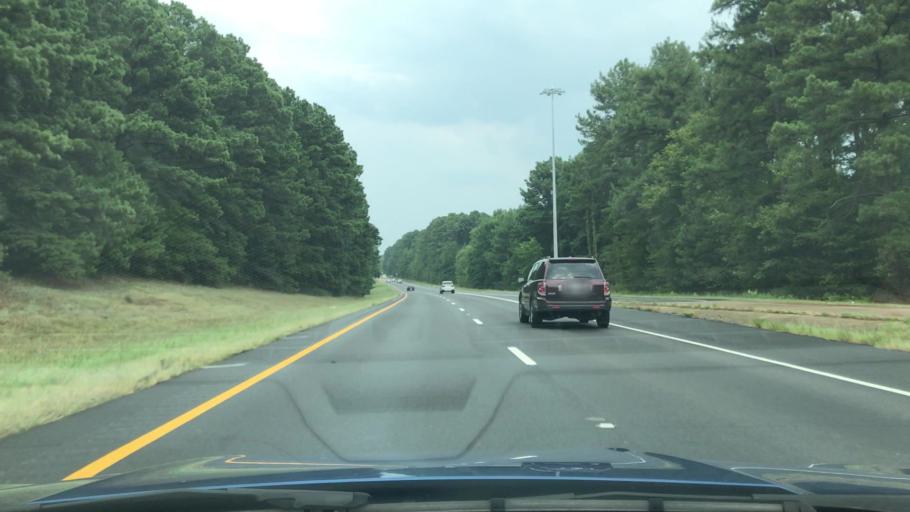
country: US
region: Texas
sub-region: Harrison County
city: Hallsville
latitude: 32.4864
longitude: -94.4664
